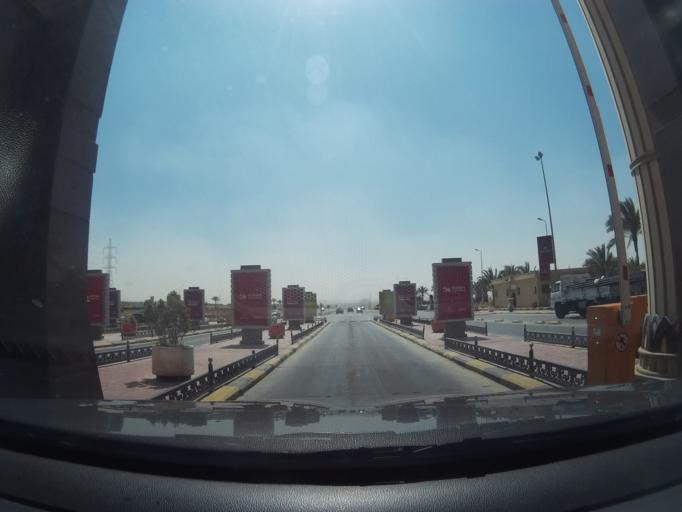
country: EG
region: As Suways
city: Ain Sukhna
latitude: 29.7652
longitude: 31.9511
